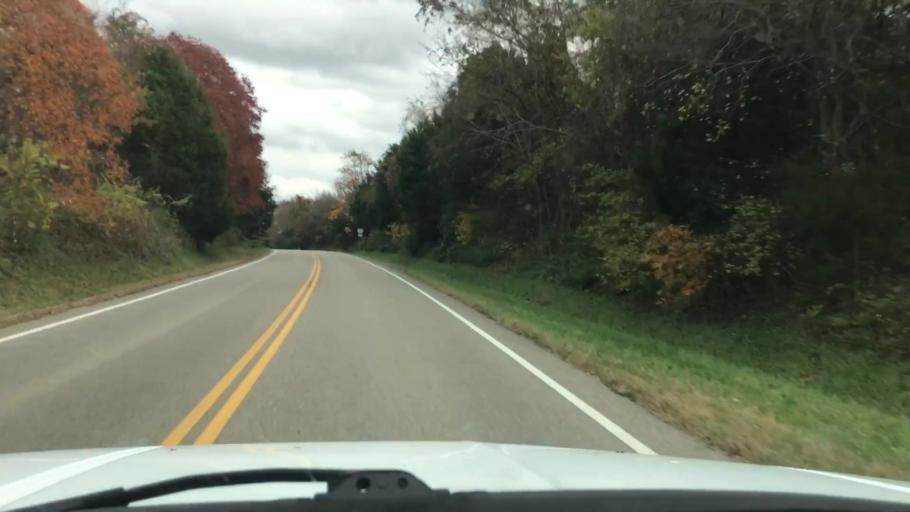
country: US
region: Virginia
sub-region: Goochland County
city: Goochland
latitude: 37.6488
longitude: -77.8386
